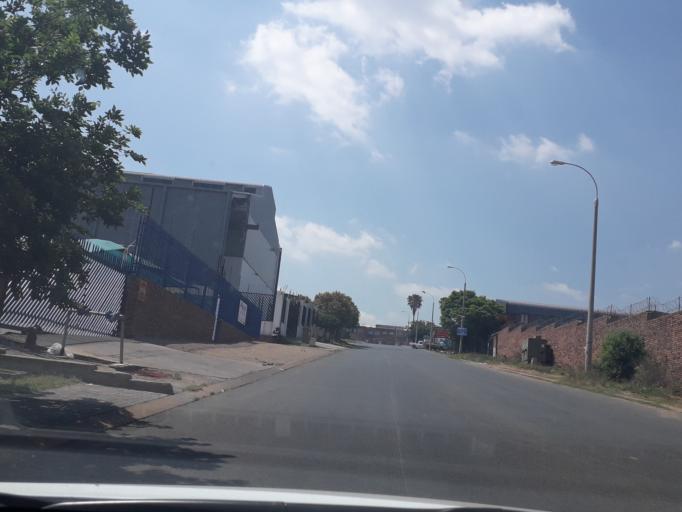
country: ZA
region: Gauteng
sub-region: West Rand District Municipality
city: Muldersdriseloop
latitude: -26.0785
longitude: 27.9122
